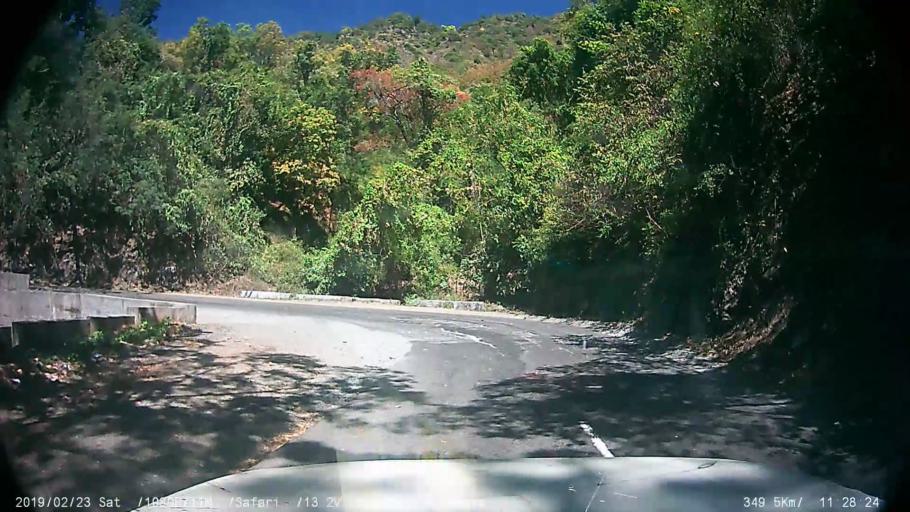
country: IN
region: Tamil Nadu
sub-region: Nilgiri
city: Kotagiri
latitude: 11.3403
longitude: 76.8646
